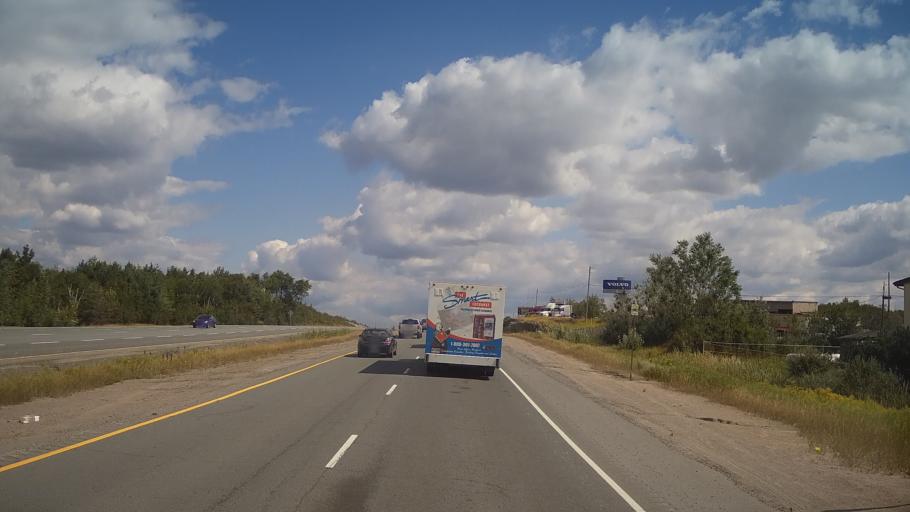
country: CA
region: Ontario
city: Greater Sudbury
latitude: 46.4366
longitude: -81.1099
